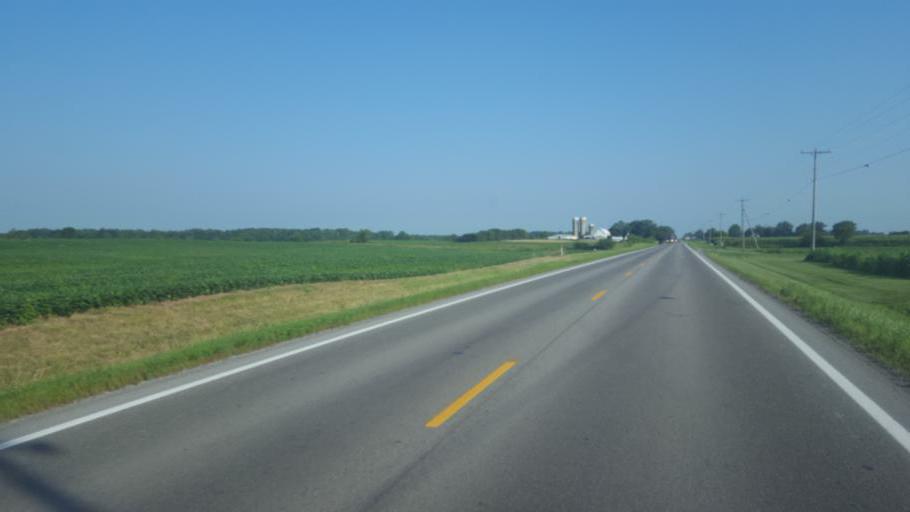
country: US
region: Ohio
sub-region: Hardin County
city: Kenton
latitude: 40.5677
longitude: -83.5483
